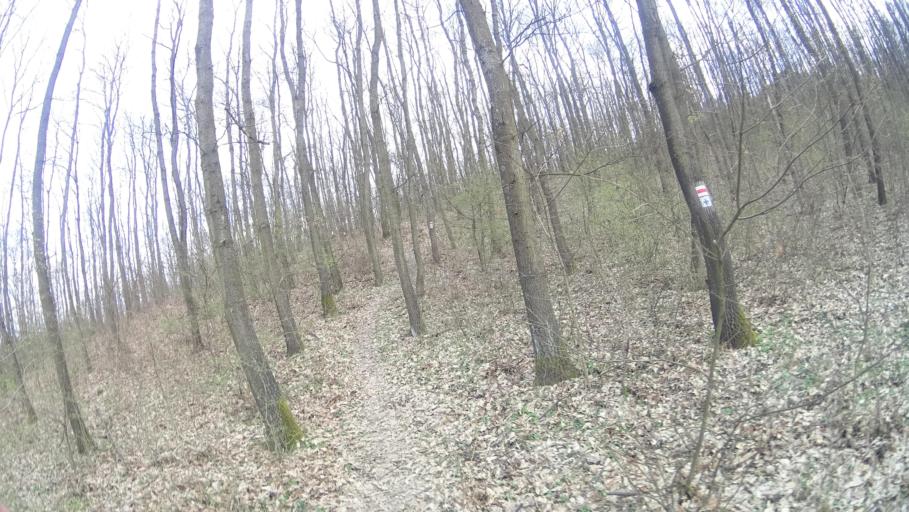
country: HU
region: Pest
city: Veroce
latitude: 47.8450
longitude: 19.1020
